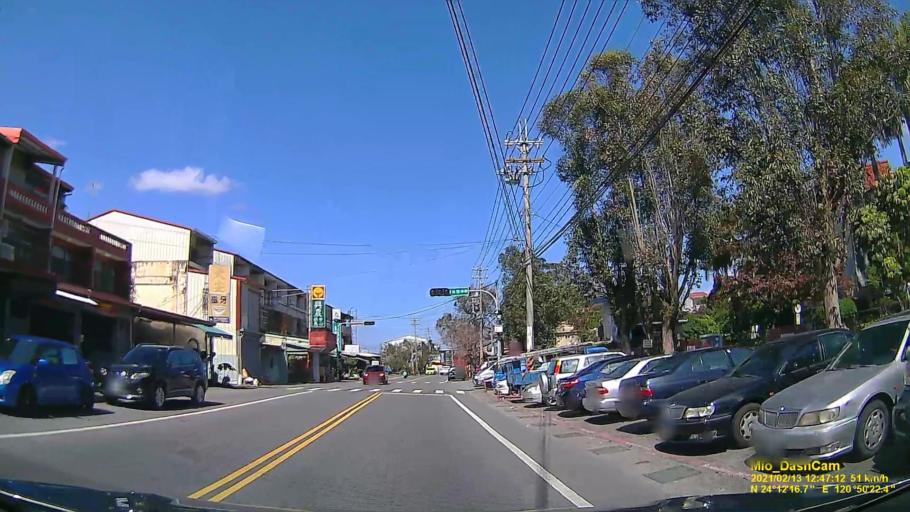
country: TW
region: Taiwan
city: Fengyuan
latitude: 24.2048
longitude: 120.8395
